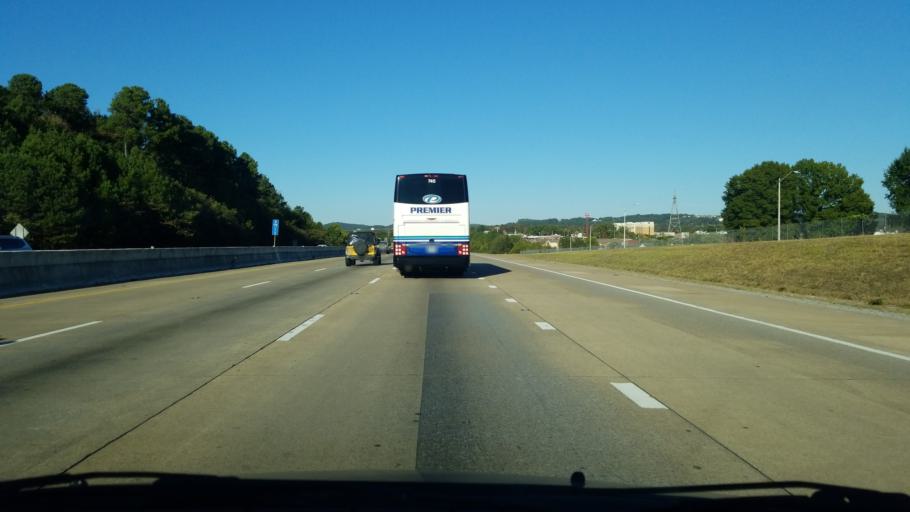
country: US
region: Tennessee
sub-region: Hamilton County
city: East Brainerd
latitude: 35.0362
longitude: -85.1625
